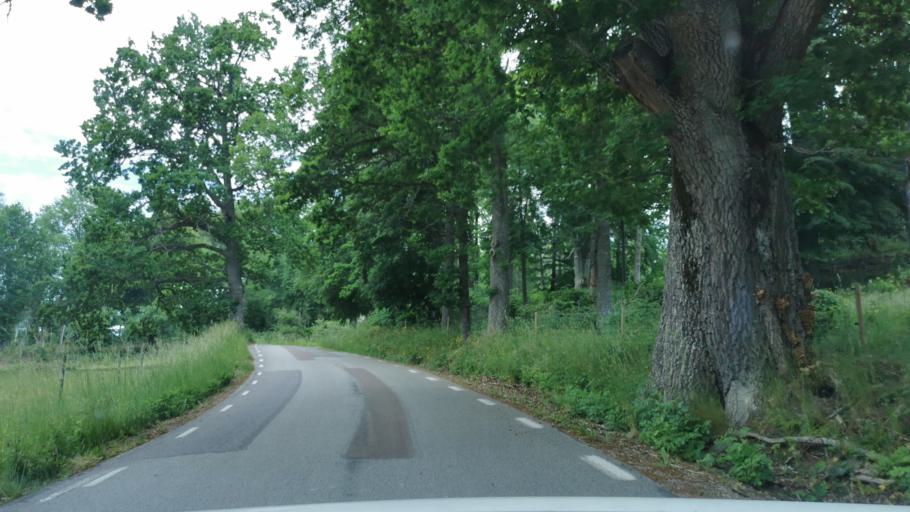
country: SE
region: Vaestra Goetaland
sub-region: Bengtsfors Kommun
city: Dals Langed
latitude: 58.8453
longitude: 12.4087
